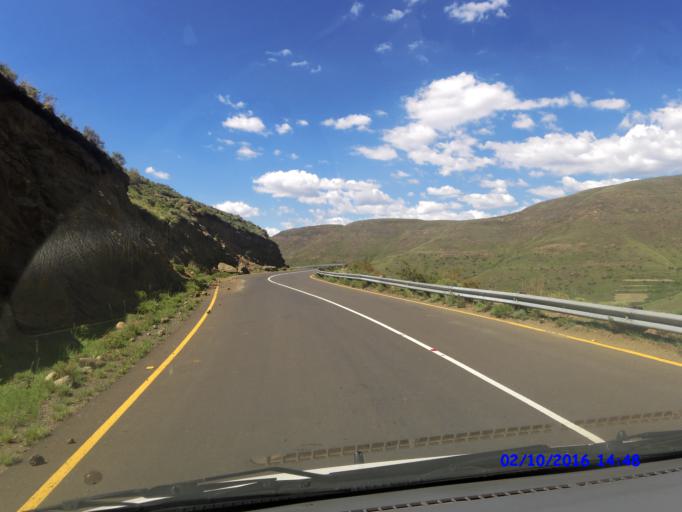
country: LS
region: Maseru
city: Nako
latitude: -29.4992
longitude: 28.0616
